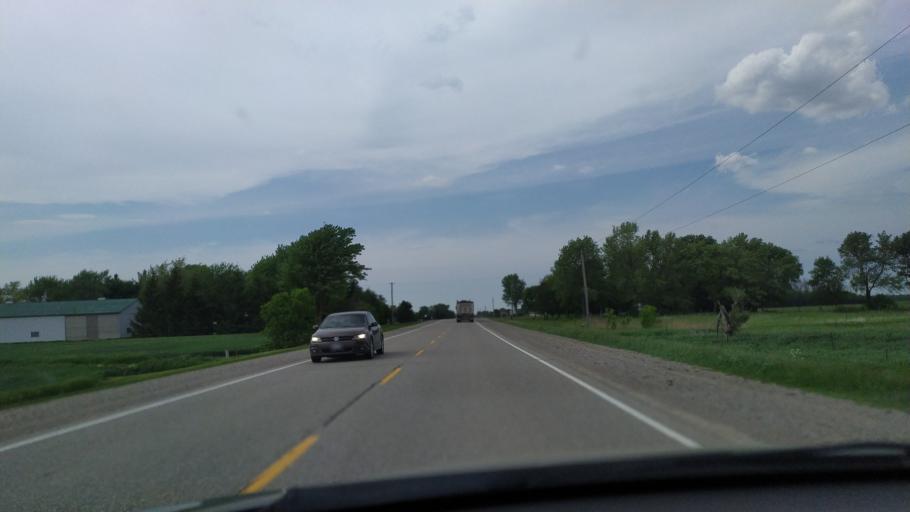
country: CA
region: Ontario
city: Stratford
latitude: 43.2344
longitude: -81.0782
